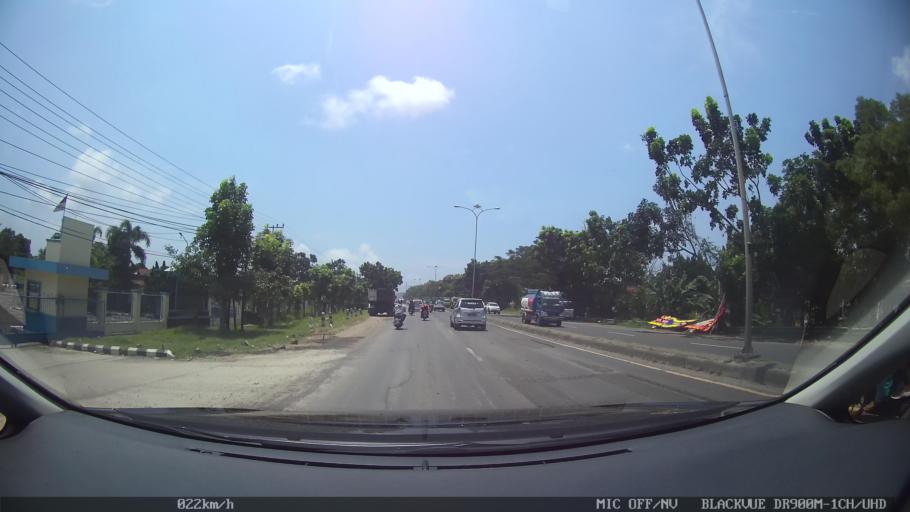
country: ID
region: Lampung
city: Kedaton
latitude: -5.3769
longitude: 105.2808
